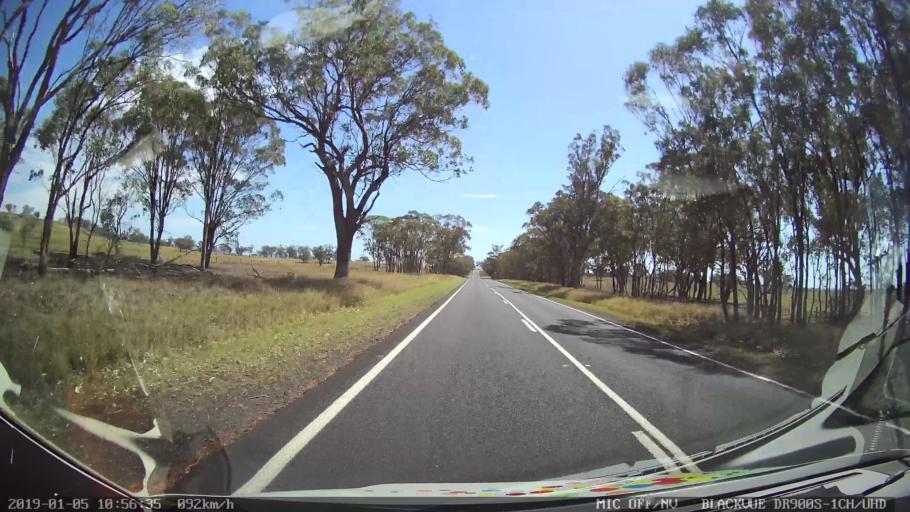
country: AU
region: New South Wales
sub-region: Warrumbungle Shire
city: Coonabarabran
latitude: -31.4399
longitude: 149.1598
